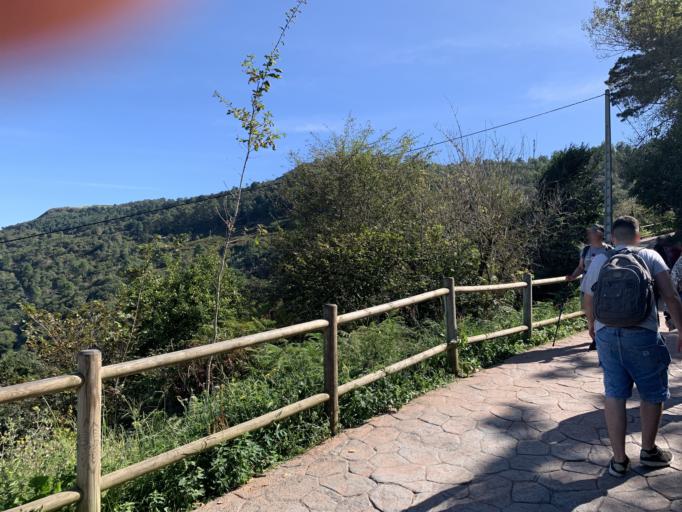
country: ES
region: Basque Country
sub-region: Bizkaia
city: Bakio
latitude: 43.4424
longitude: -2.7829
